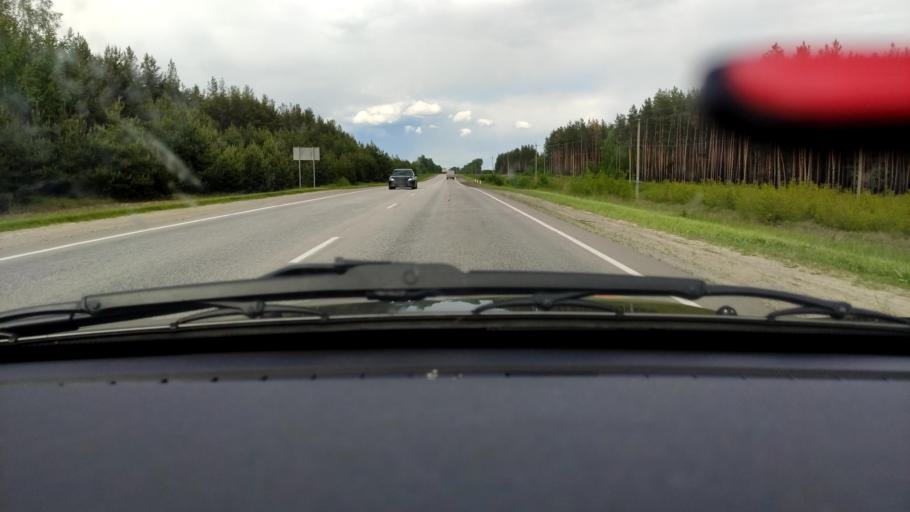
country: RU
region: Voronezj
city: Uryv-Pokrovka
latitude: 51.0543
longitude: 38.9871
